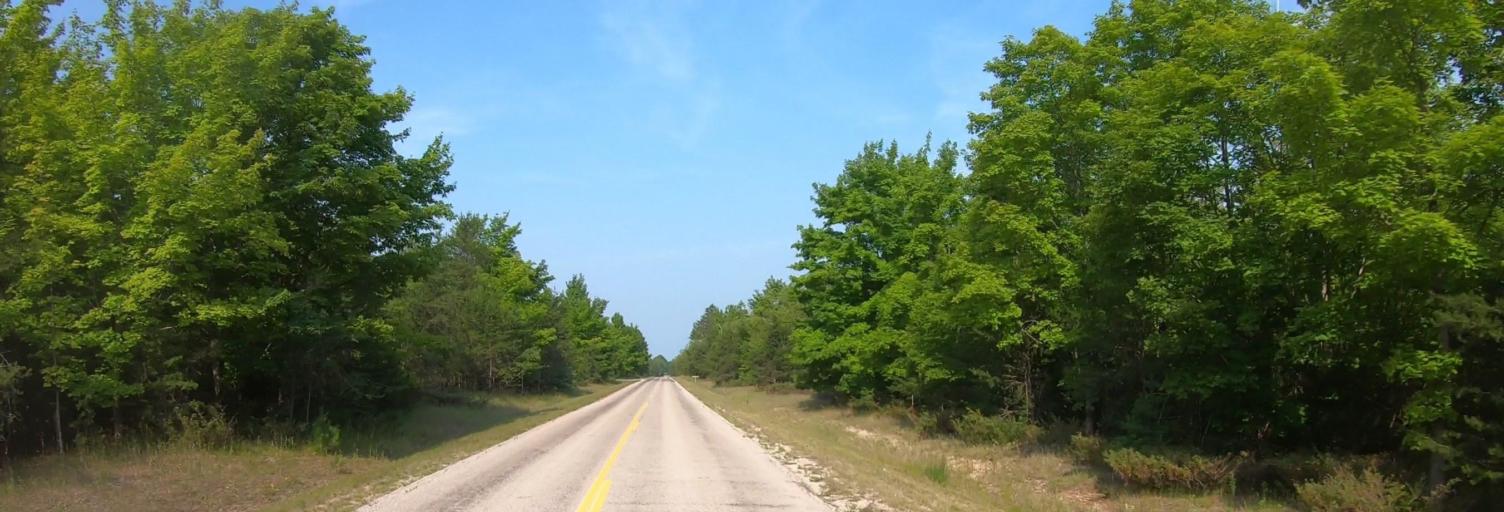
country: US
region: Michigan
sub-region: Benzie County
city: Beulah
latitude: 44.7784
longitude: -85.9453
